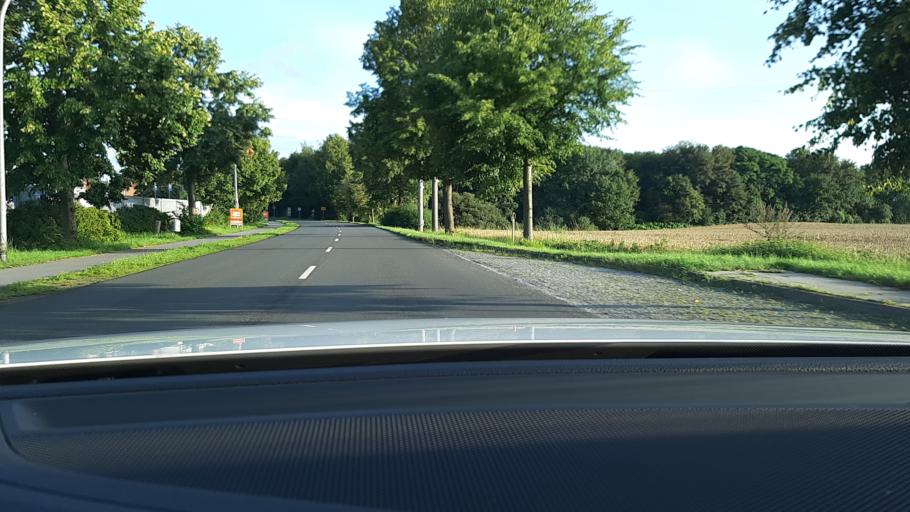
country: DE
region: Schleswig-Holstein
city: Stockelsdorf
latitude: 53.9040
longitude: 10.6415
